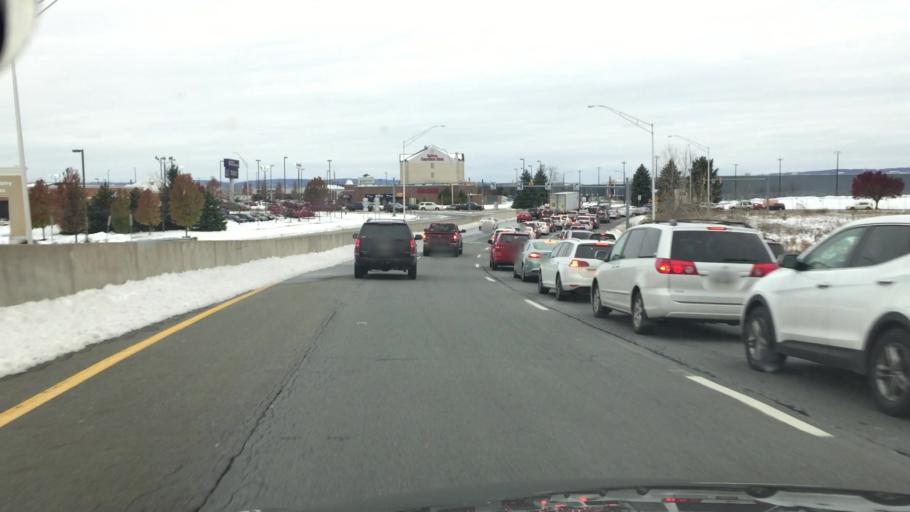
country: US
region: Pennsylvania
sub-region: Luzerne County
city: Georgetown
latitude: 41.2370
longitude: -75.8521
